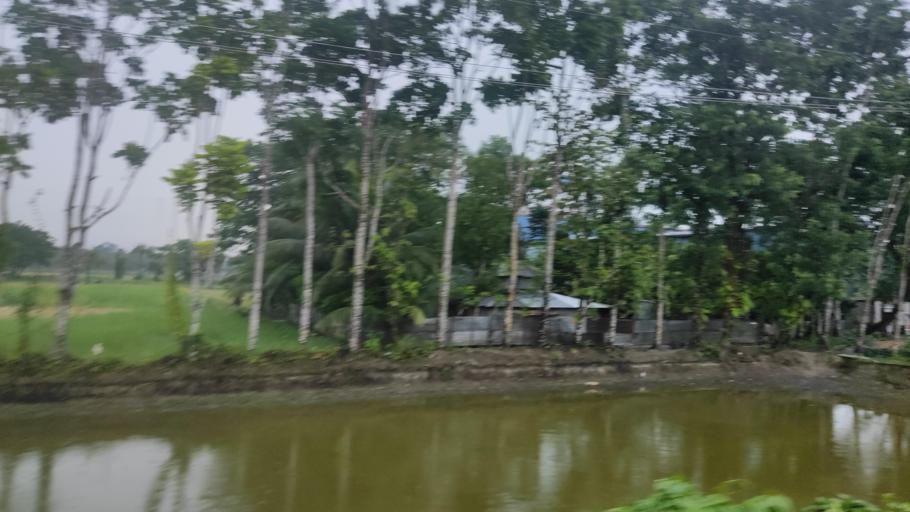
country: BD
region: Barisal
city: Bhandaria
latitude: 22.3096
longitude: 90.3250
